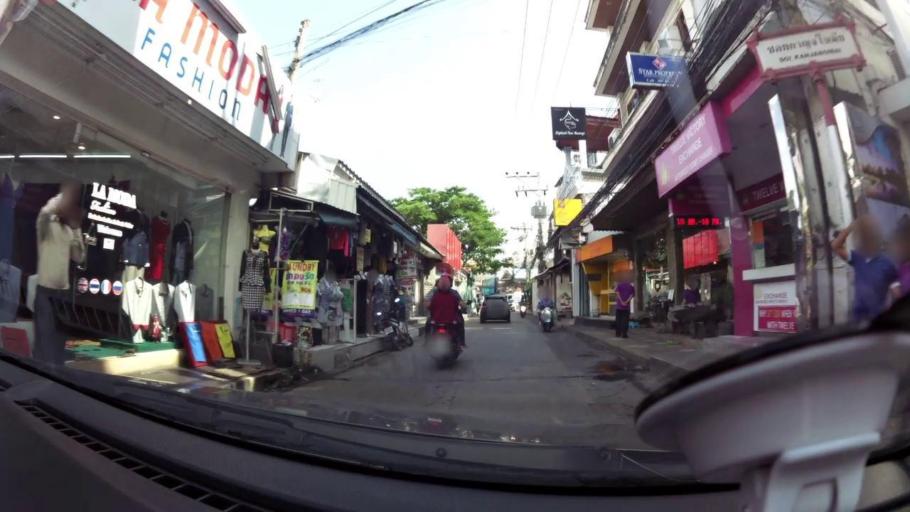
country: TH
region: Prachuap Khiri Khan
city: Hua Hin
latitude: 12.5694
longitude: 99.9599
